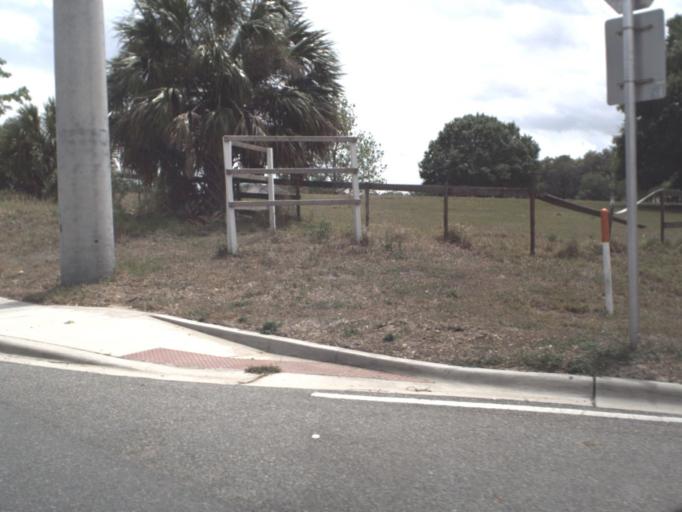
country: US
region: Florida
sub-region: Orange County
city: Oakland
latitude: 28.5461
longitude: -81.6572
